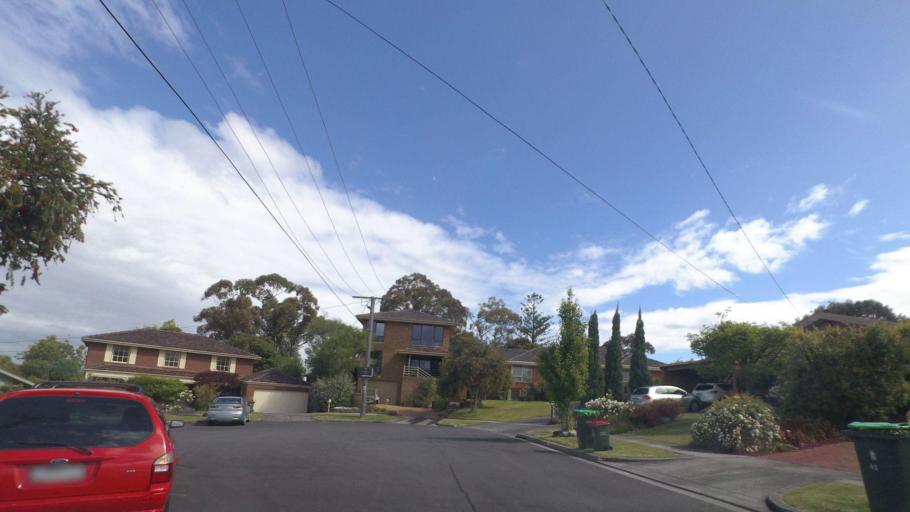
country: AU
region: Victoria
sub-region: Whitehorse
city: Vermont
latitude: -37.8313
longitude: 145.1989
